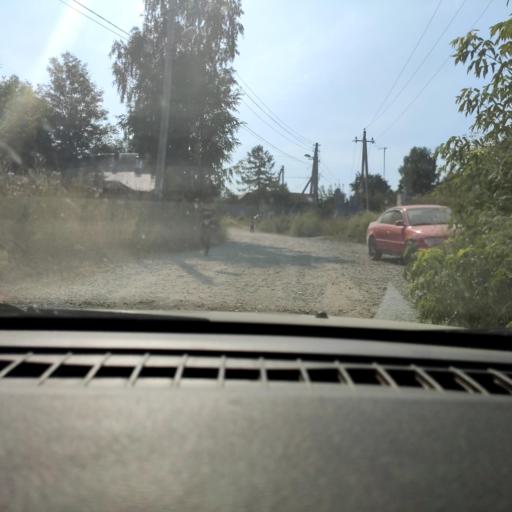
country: RU
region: Perm
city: Polazna
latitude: 58.1446
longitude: 56.4566
